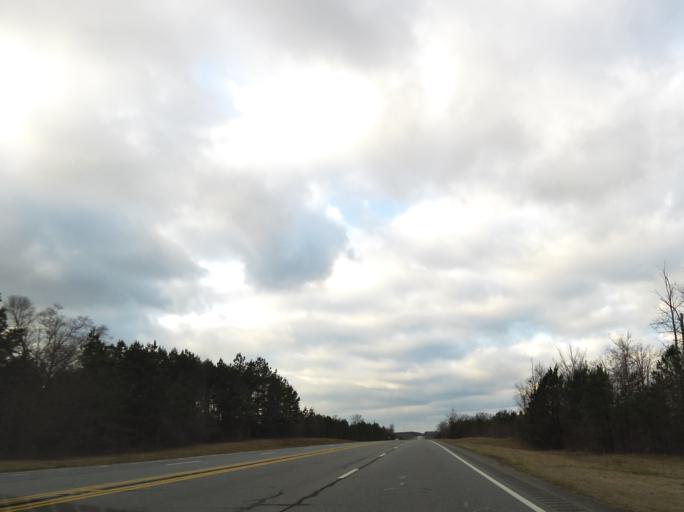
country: US
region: Georgia
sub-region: Bleckley County
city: Cochran
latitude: 32.4719
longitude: -83.3901
